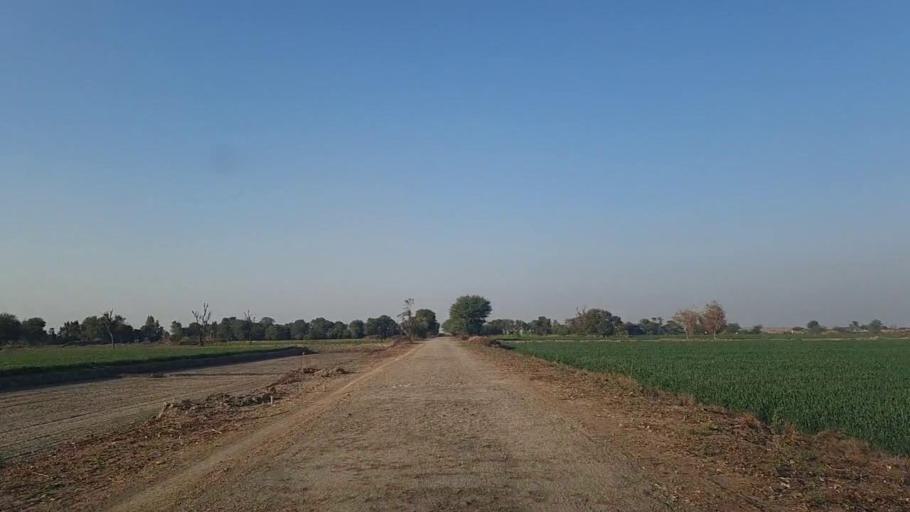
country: PK
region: Sindh
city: Jam Sahib
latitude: 26.3043
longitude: 68.6704
